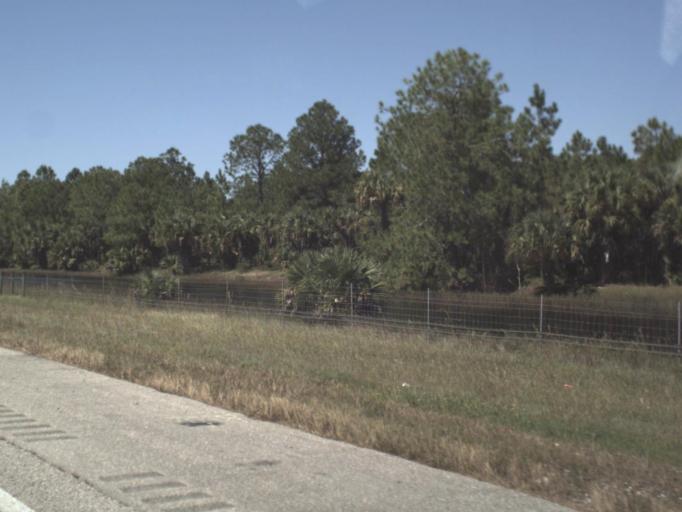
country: US
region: Florida
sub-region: Collier County
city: Golden Gate
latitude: 26.1534
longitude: -81.5748
